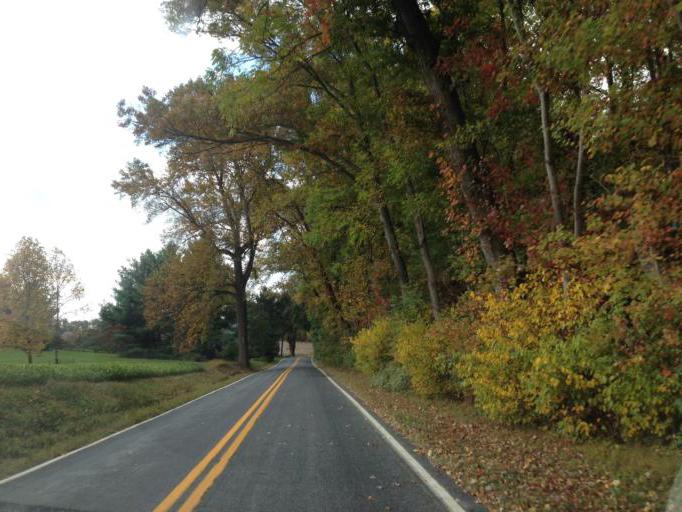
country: US
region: Maryland
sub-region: Carroll County
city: Mount Airy
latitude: 39.3186
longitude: -77.1292
